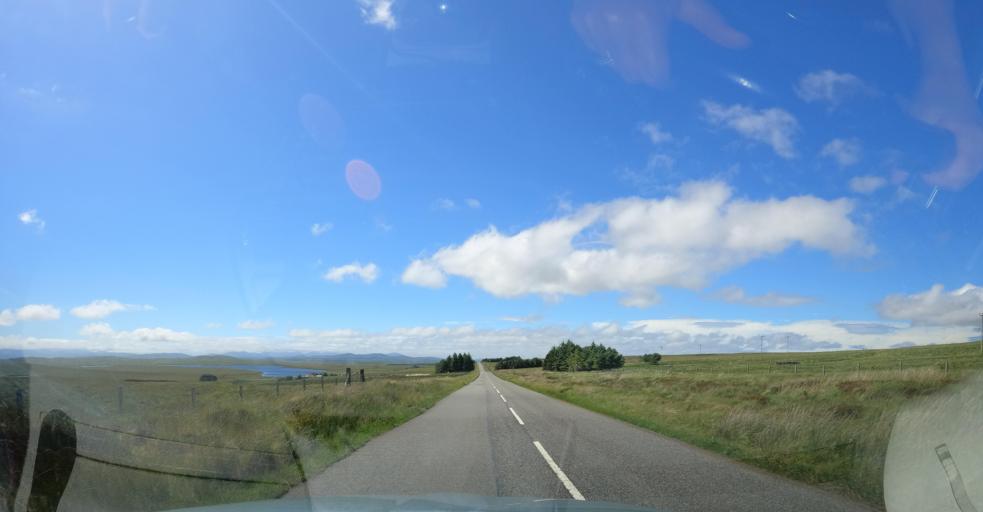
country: GB
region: Scotland
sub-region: Eilean Siar
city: Stornoway
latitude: 58.1731
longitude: -6.5950
